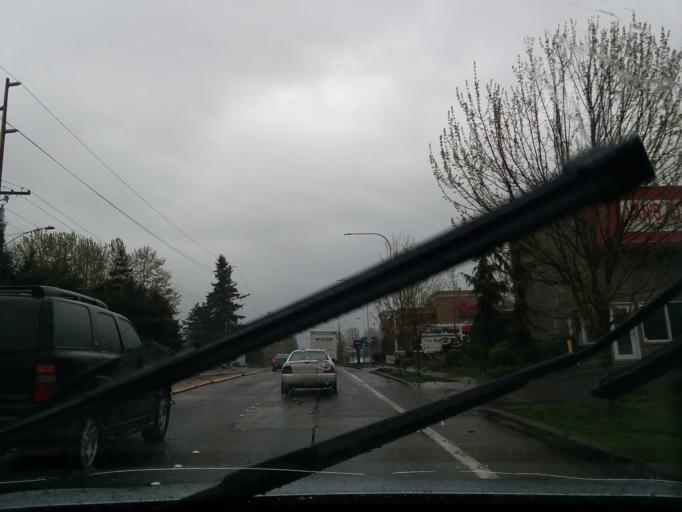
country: US
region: Washington
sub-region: King County
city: Fairwood
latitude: 47.4885
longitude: -122.1603
